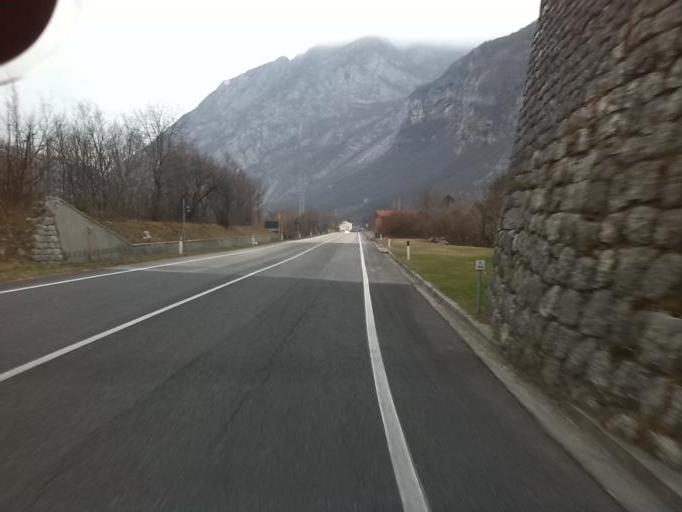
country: IT
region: Friuli Venezia Giulia
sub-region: Provincia di Udine
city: Venzone
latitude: 46.3342
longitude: 13.1373
